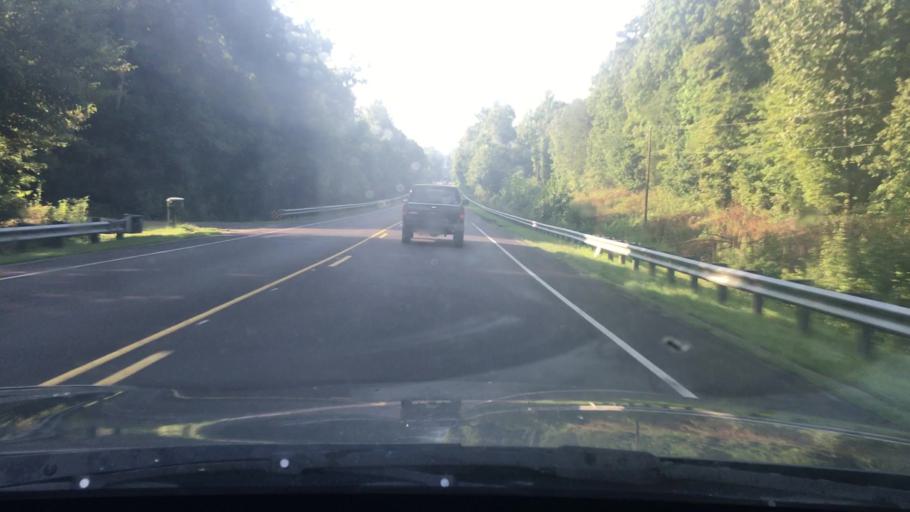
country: US
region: North Carolina
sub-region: Caswell County
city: Yanceyville
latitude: 36.4857
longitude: -79.3819
